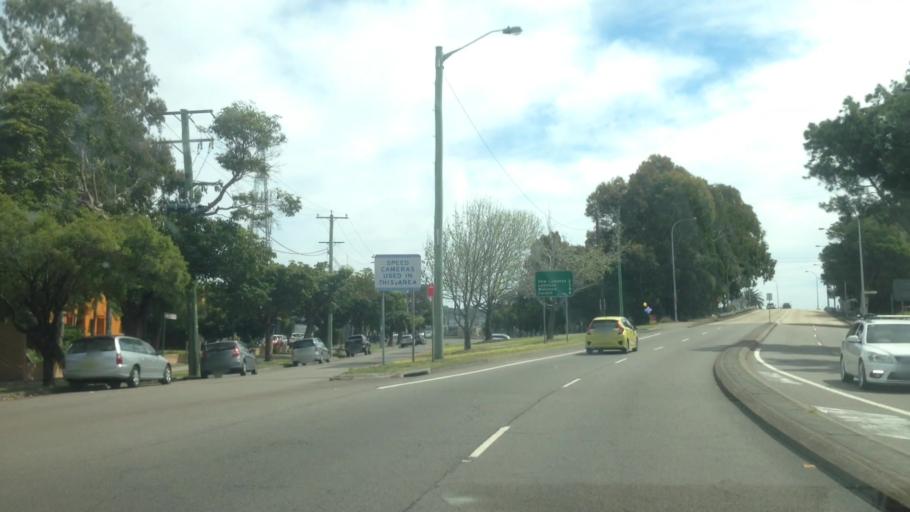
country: AU
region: New South Wales
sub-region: Newcastle
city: Broadmeadow
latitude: -32.9246
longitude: 151.7359
